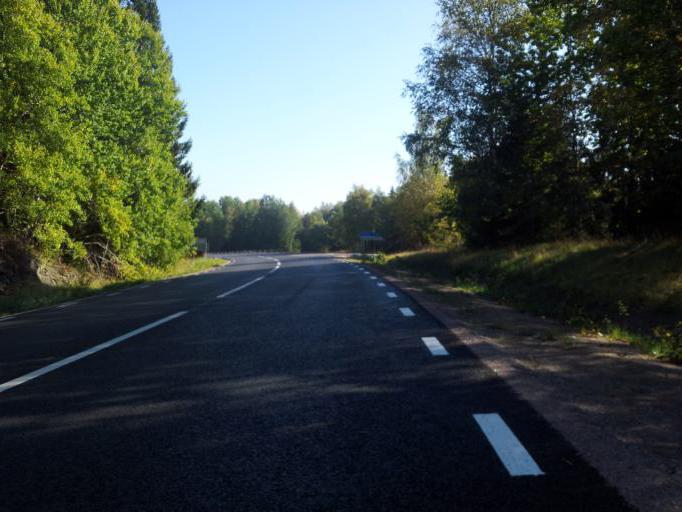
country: SE
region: Stockholm
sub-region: Norrtalje Kommun
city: Nykvarn
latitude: 59.8566
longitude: 18.1005
